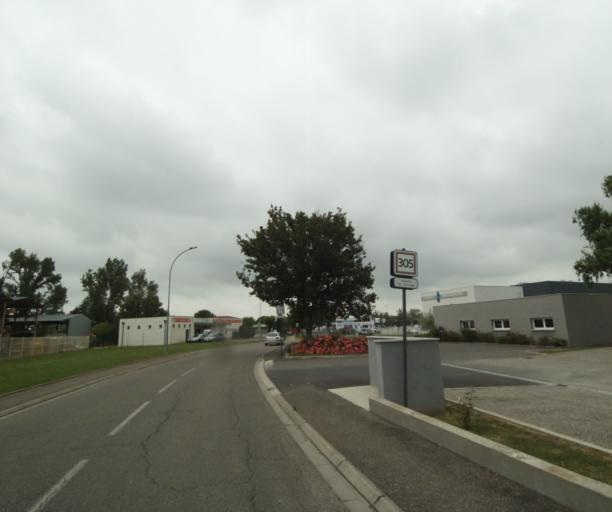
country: FR
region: Midi-Pyrenees
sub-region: Departement du Tarn-et-Garonne
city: Montauban
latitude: 43.9963
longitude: 1.3343
